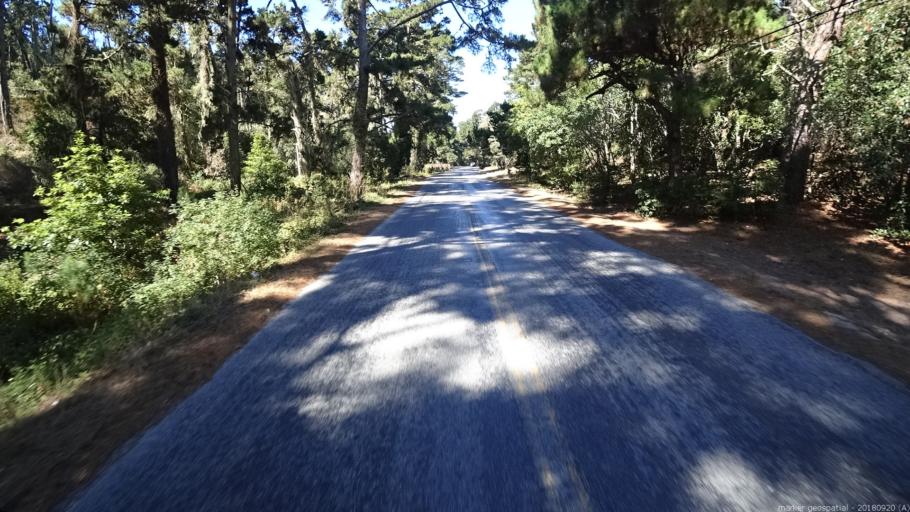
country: US
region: California
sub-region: Monterey County
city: Carmel-by-the-Sea
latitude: 36.5723
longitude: -121.9068
